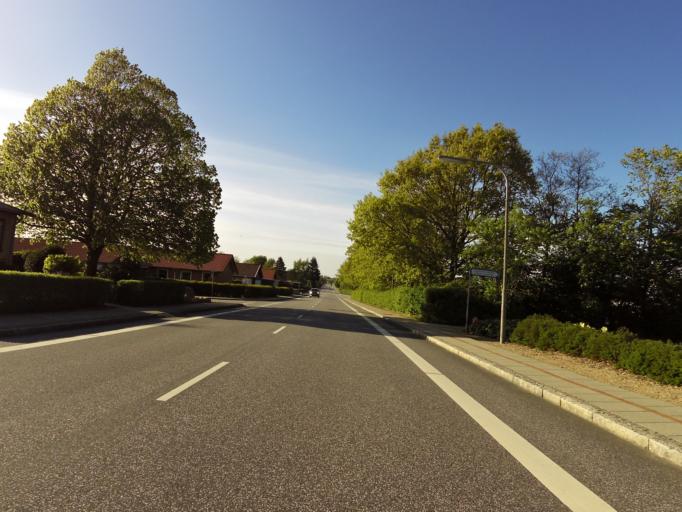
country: DK
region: South Denmark
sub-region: Tonder Kommune
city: Toftlund
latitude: 55.1859
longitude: 9.0634
